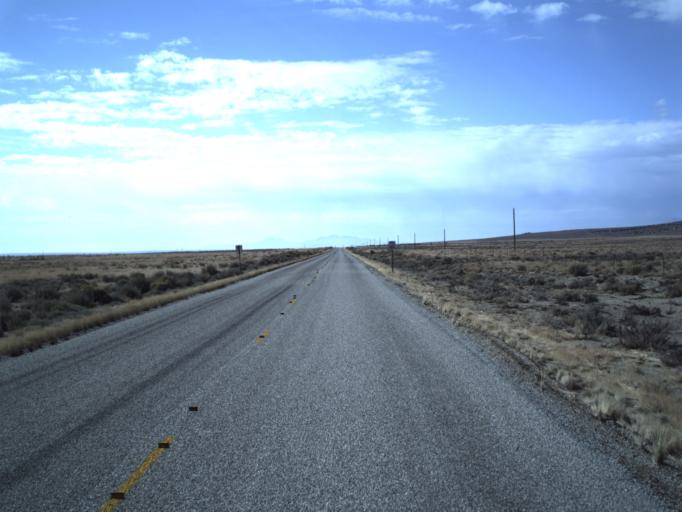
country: US
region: Utah
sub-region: Tooele County
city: Wendover
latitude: 41.5514
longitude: -113.5865
